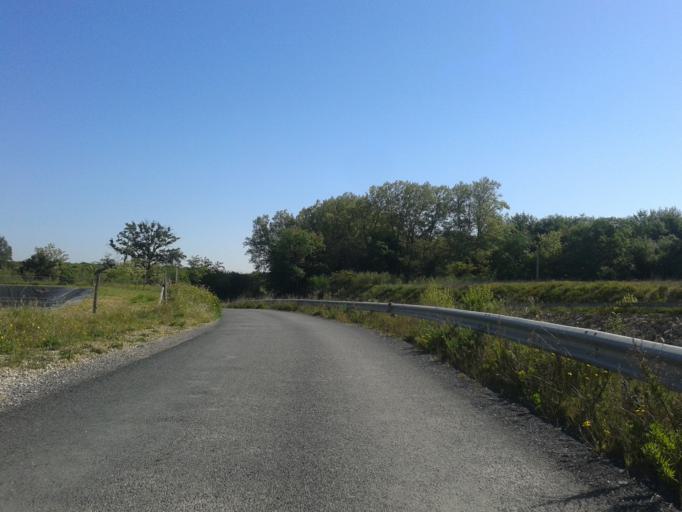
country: FR
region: Languedoc-Roussillon
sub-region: Departement des Pyrenees-Orientales
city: Toulouges
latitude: 42.6735
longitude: 2.8165
